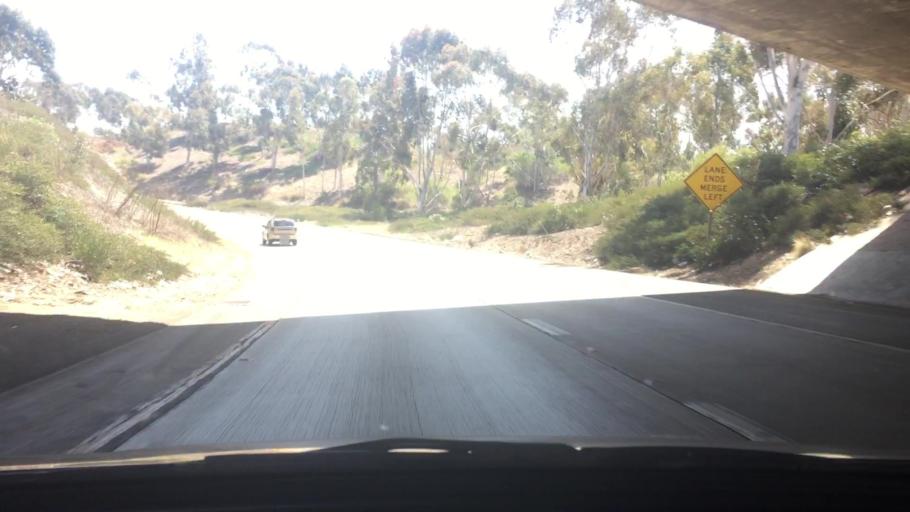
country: US
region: California
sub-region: San Diego County
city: National City
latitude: 32.7187
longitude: -117.1042
